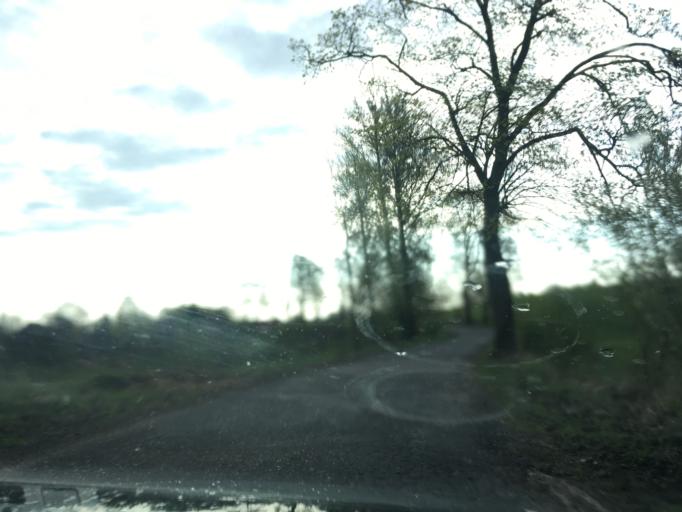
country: PL
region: Warmian-Masurian Voivodeship
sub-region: Powiat ostrodzki
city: Dabrowno
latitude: 53.4282
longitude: 20.0116
